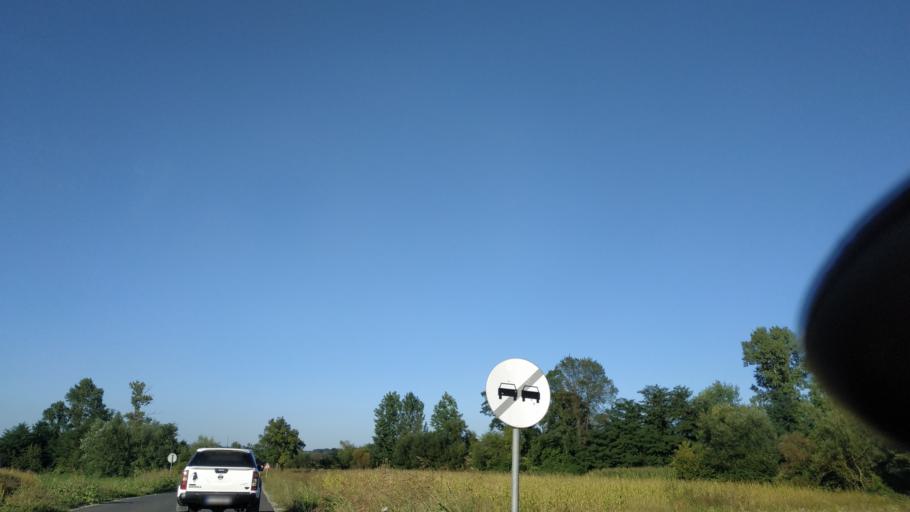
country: RS
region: Central Serbia
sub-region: Rasinski Okrug
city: Krusevac
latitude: 43.5251
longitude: 21.3355
